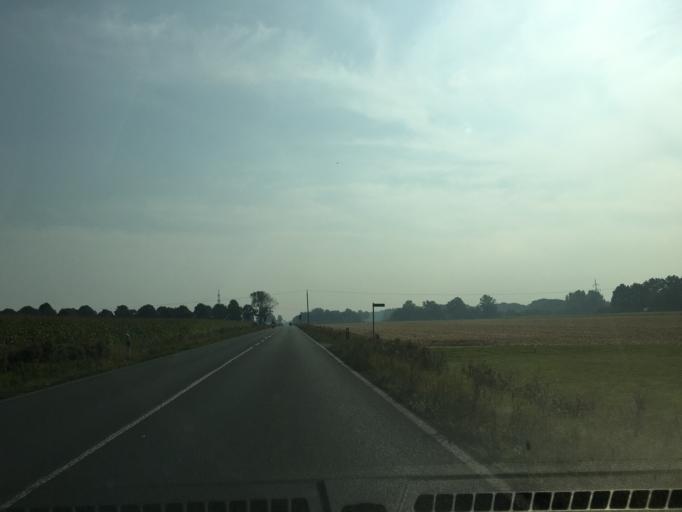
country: DE
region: North Rhine-Westphalia
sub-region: Regierungsbezirk Munster
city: Dulmen
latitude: 51.7862
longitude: 7.3494
